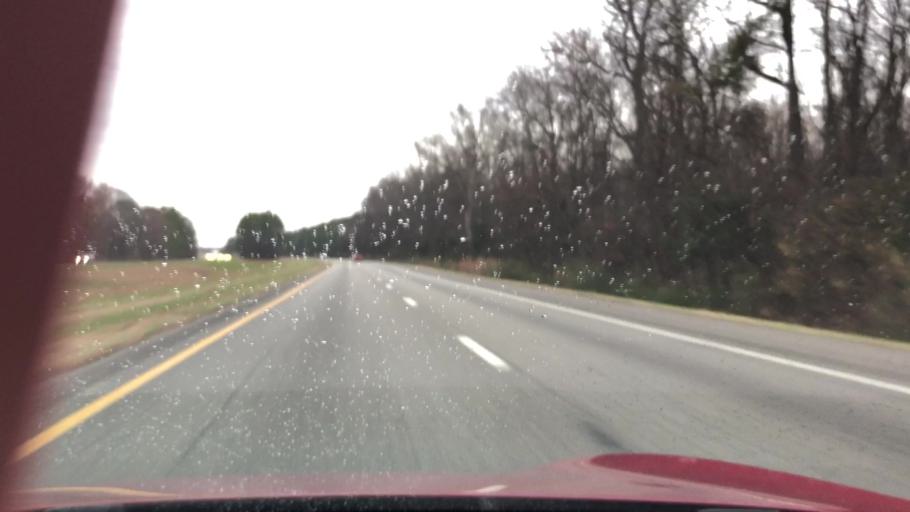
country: US
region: South Carolina
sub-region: Dillon County
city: Latta
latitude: 34.3574
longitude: -79.5090
